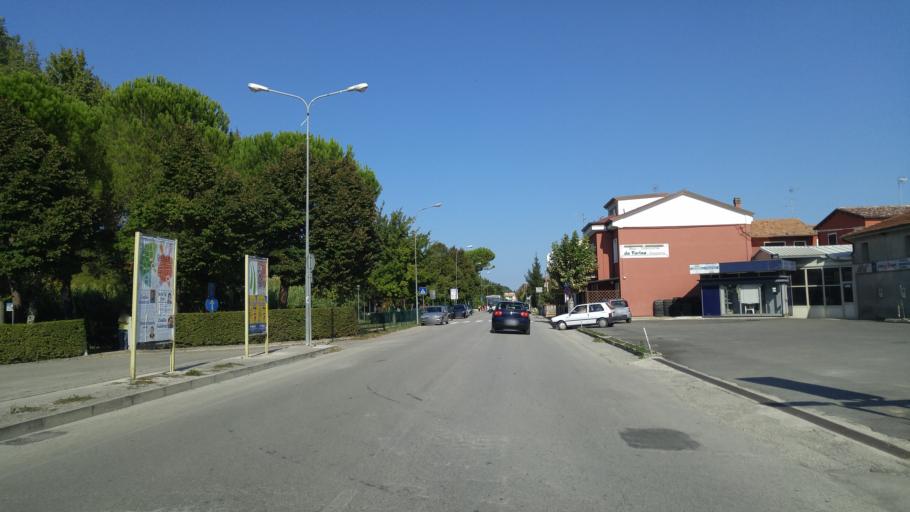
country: IT
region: The Marches
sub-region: Provincia di Pesaro e Urbino
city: Cuccurano
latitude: 43.7940
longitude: 12.9552
